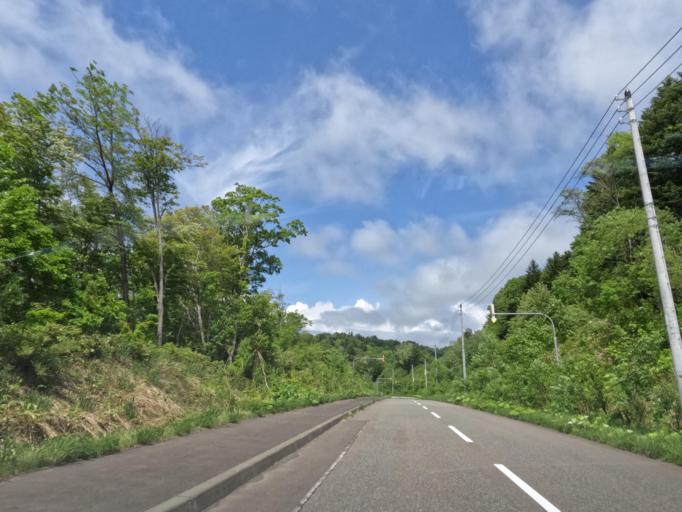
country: JP
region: Hokkaido
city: Tobetsu
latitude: 43.3524
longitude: 141.5689
